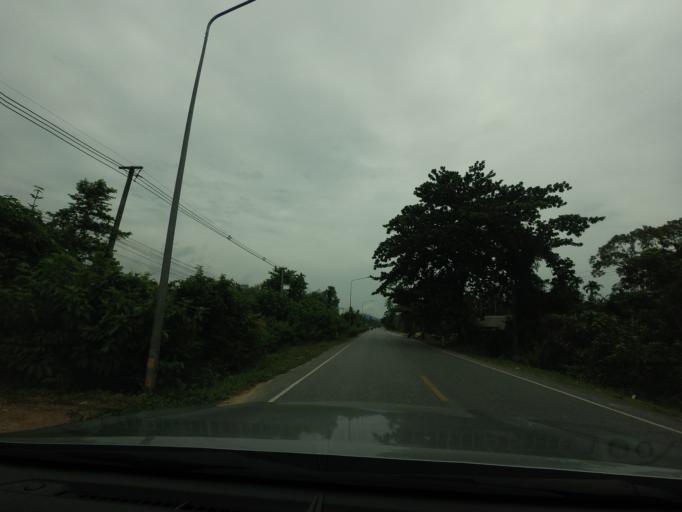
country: TH
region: Yala
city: Raman
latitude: 6.4087
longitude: 101.3688
